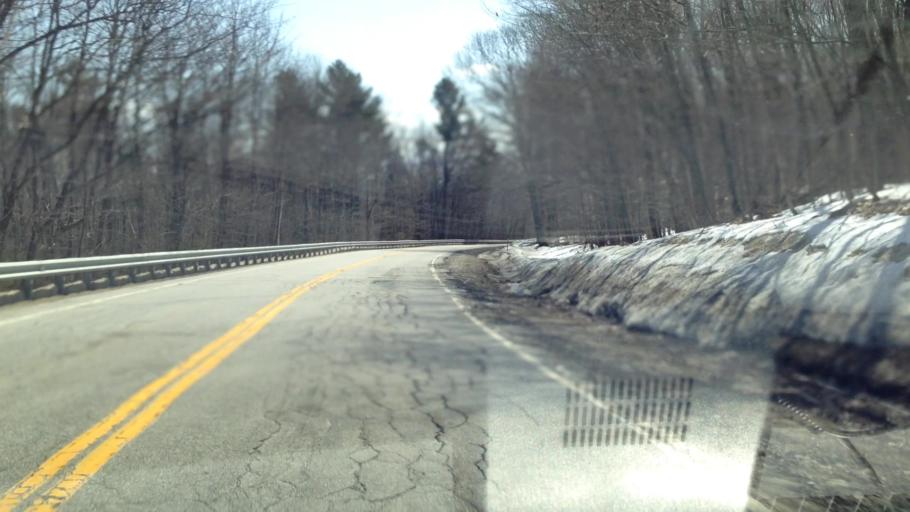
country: US
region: New Hampshire
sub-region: Sullivan County
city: Springfield
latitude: 43.4892
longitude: -71.9803
